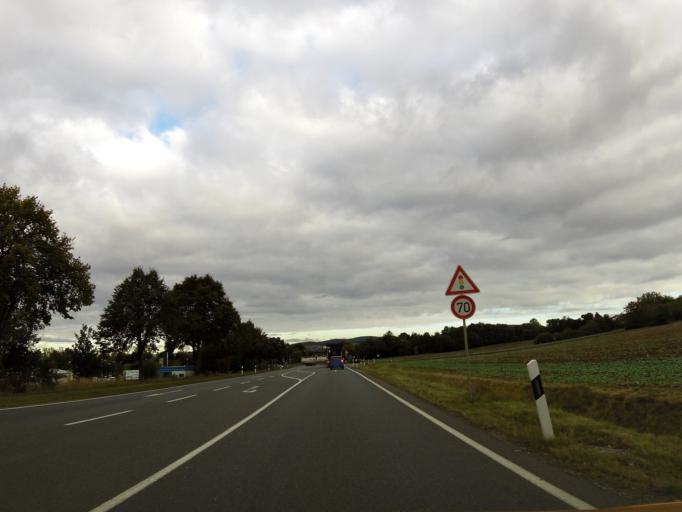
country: DE
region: Lower Saxony
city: Northeim
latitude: 51.7303
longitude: 9.9746
